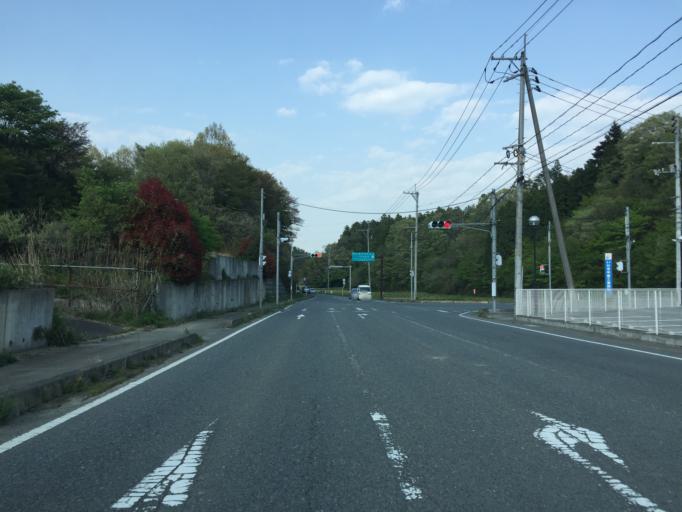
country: JP
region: Fukushima
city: Iwaki
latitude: 36.9746
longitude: 140.8412
